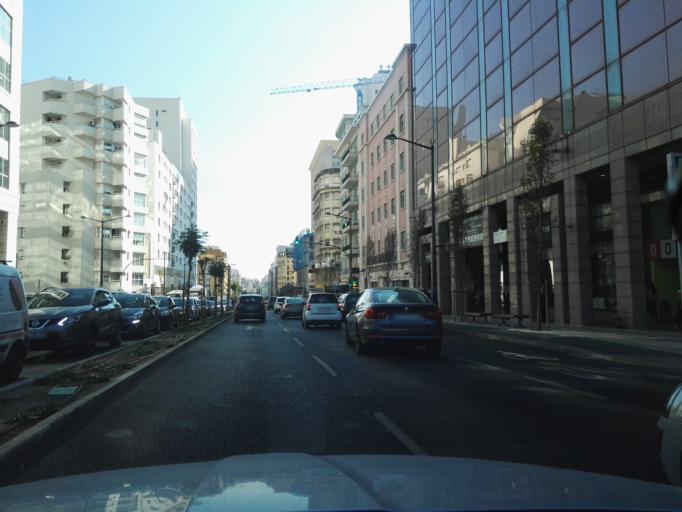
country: PT
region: Lisbon
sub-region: Lisbon
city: Lisbon
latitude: 38.7333
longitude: -9.1452
